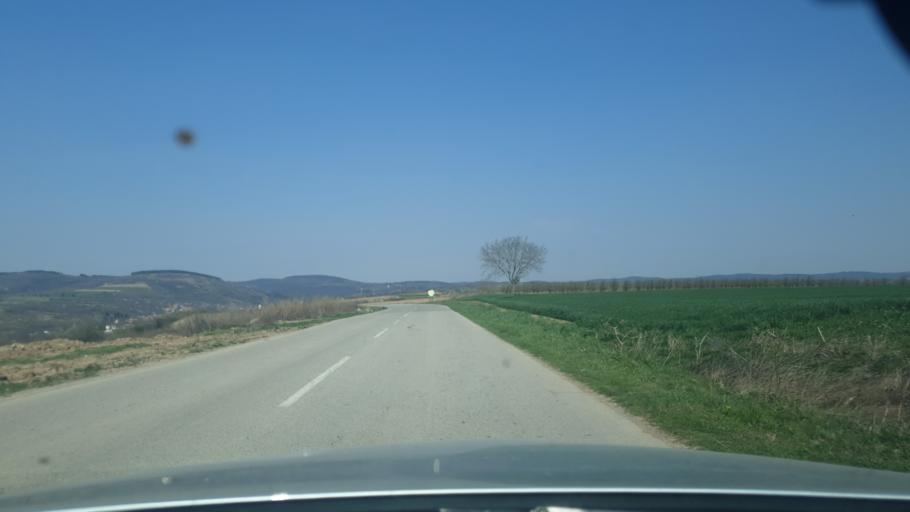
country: RS
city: Vrdnik
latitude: 45.0852
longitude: 19.7690
